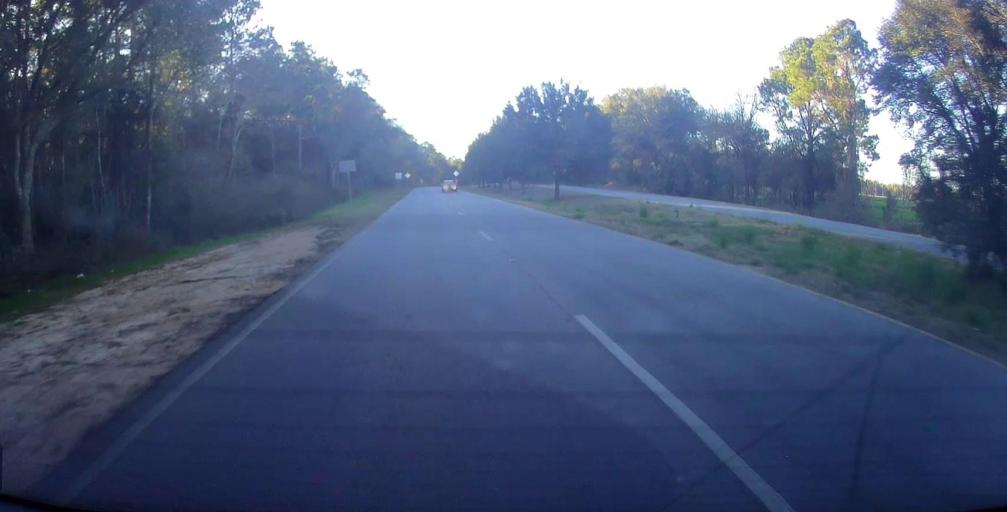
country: US
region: Georgia
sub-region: Dougherty County
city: Albany
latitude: 31.5335
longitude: -84.2177
